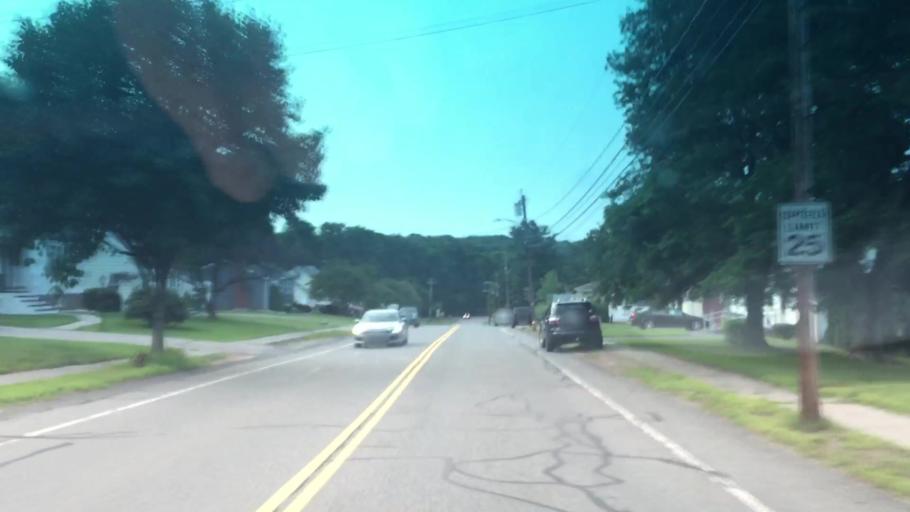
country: US
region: Massachusetts
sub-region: Norfolk County
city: Norwood
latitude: 42.2013
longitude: -71.1953
